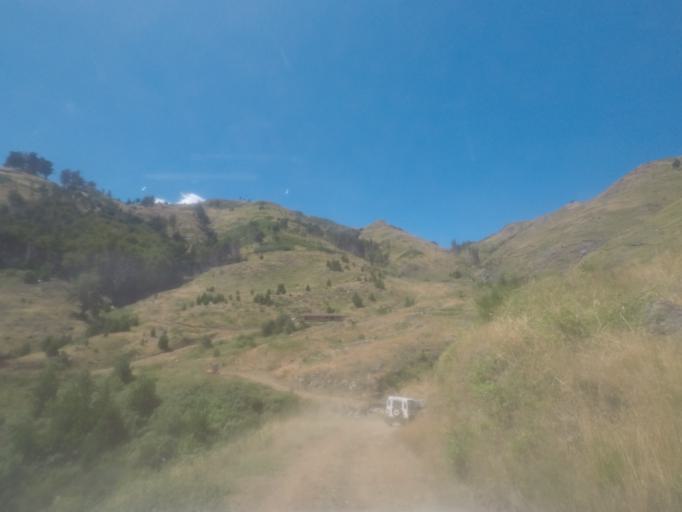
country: PT
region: Madeira
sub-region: Funchal
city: Nossa Senhora do Monte
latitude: 32.7048
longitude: -16.9013
